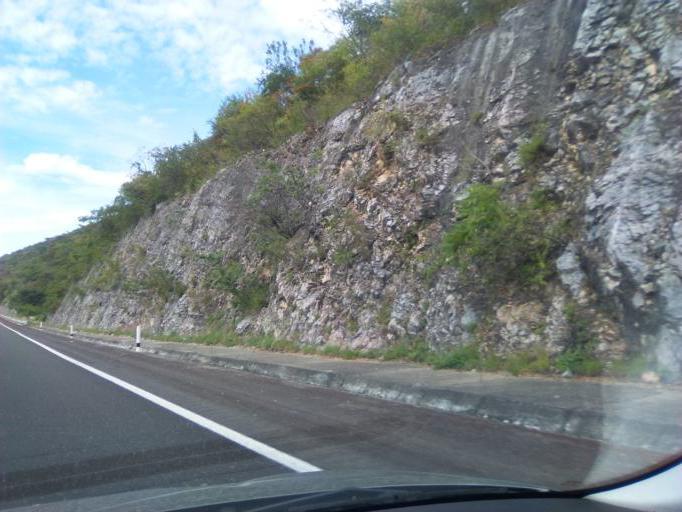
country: MX
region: Guerrero
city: Huitziltepec
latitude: 17.7807
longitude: -99.4823
